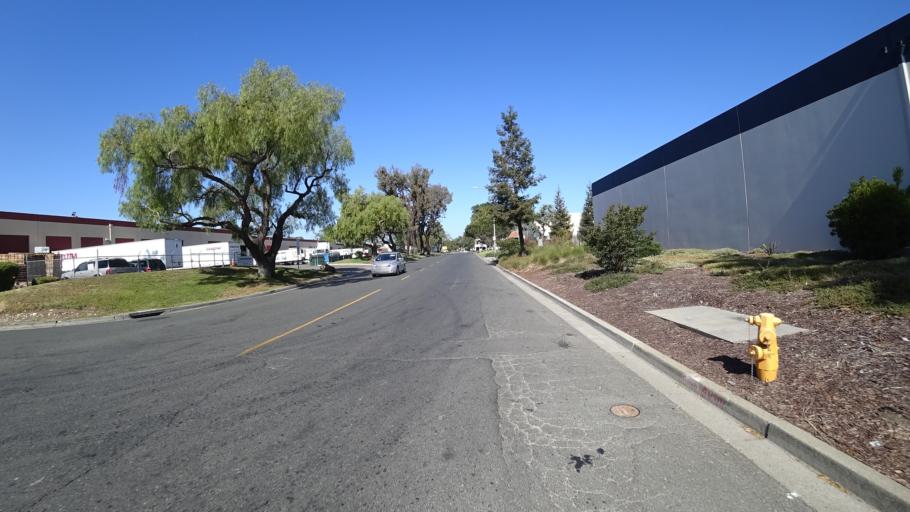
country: US
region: California
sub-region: Alameda County
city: Union City
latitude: 37.6194
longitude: -122.0526
